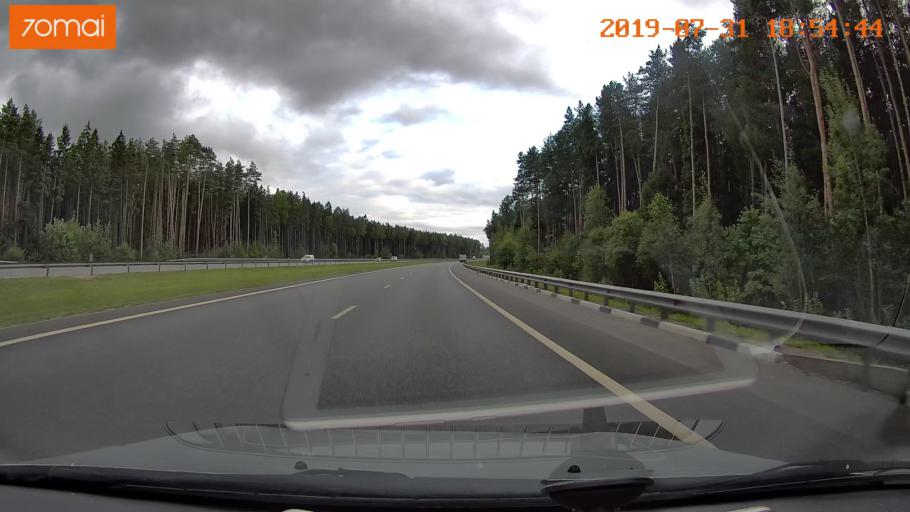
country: RU
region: Moskovskaya
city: Raduzhnyy
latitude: 55.1852
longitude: 38.6695
